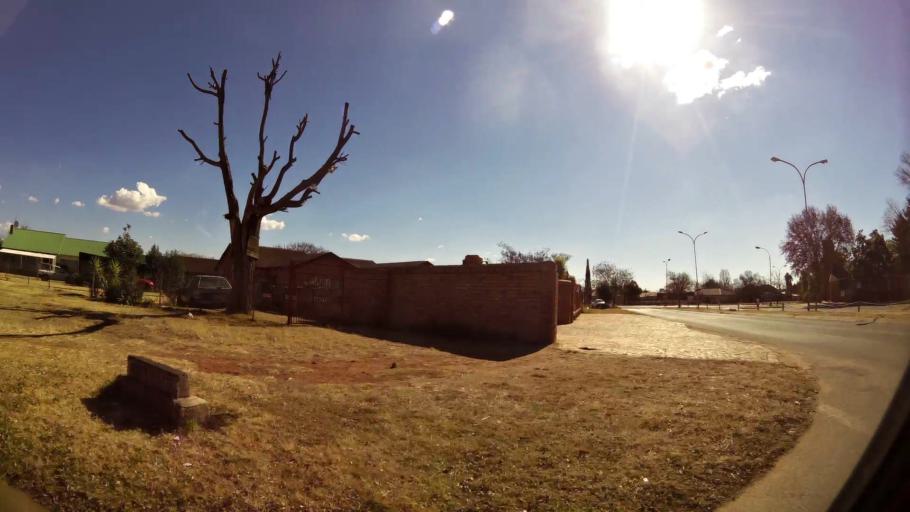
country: ZA
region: Gauteng
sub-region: West Rand District Municipality
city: Carletonville
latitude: -26.3628
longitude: 27.3944
